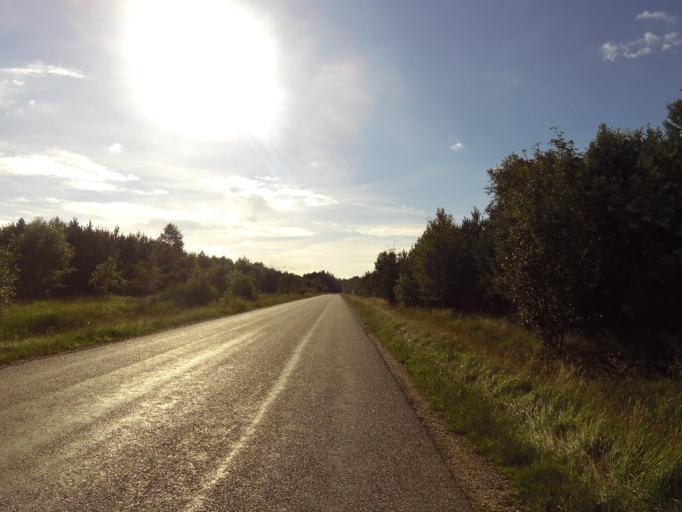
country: DK
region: South Denmark
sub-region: Haderslev Kommune
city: Vojens
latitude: 55.2101
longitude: 9.2464
